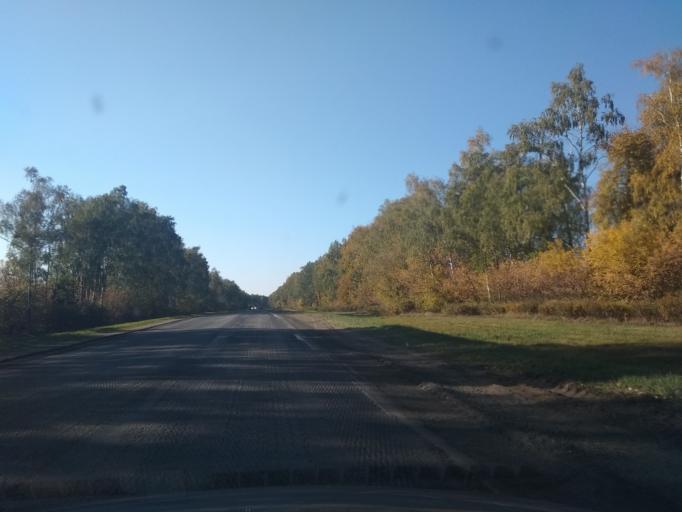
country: BY
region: Grodnenskaya
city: Zhyrovichy
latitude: 53.0585
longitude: 25.4475
